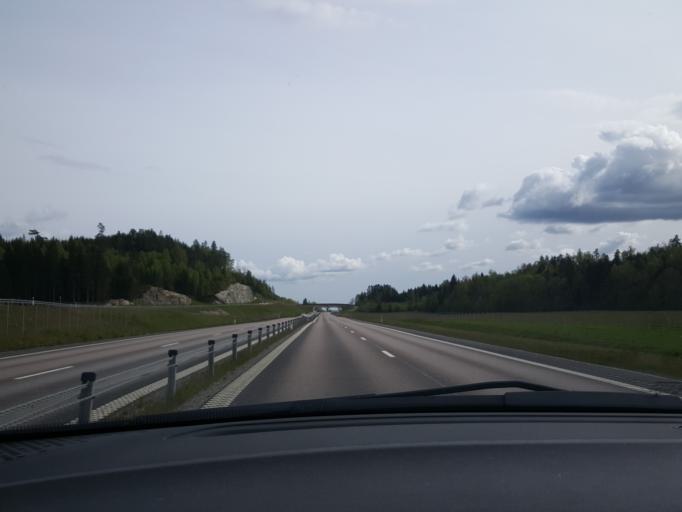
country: SE
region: Vaestra Goetaland
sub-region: Lilla Edets Kommun
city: Lilla Edet
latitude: 58.1760
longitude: 12.1402
